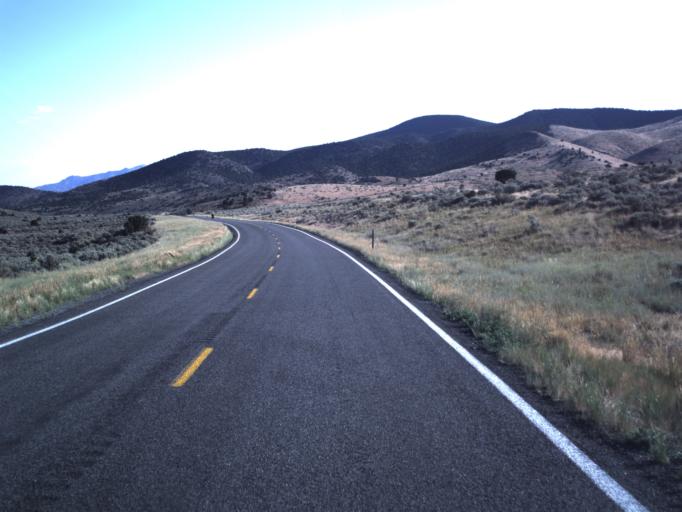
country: US
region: Utah
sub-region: Iron County
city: Parowan
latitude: 38.0920
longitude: -112.9512
